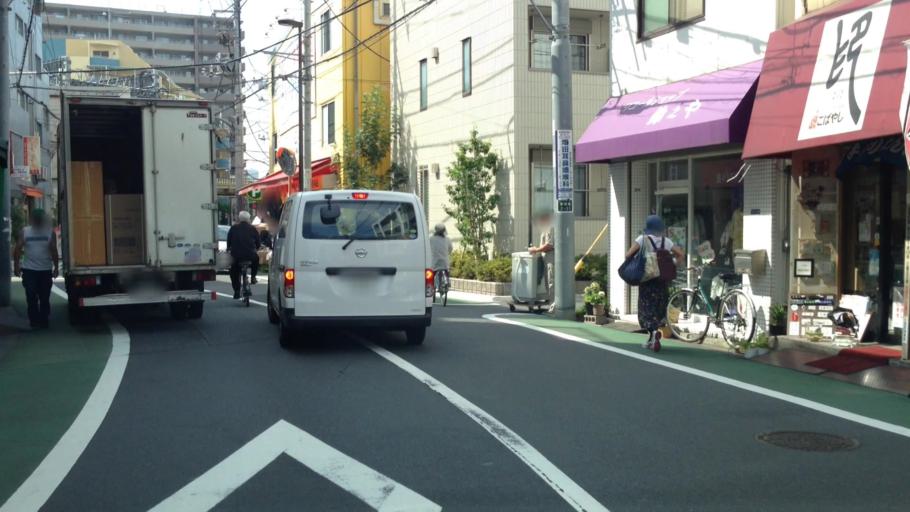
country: JP
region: Tokyo
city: Urayasu
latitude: 35.7189
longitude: 139.8177
